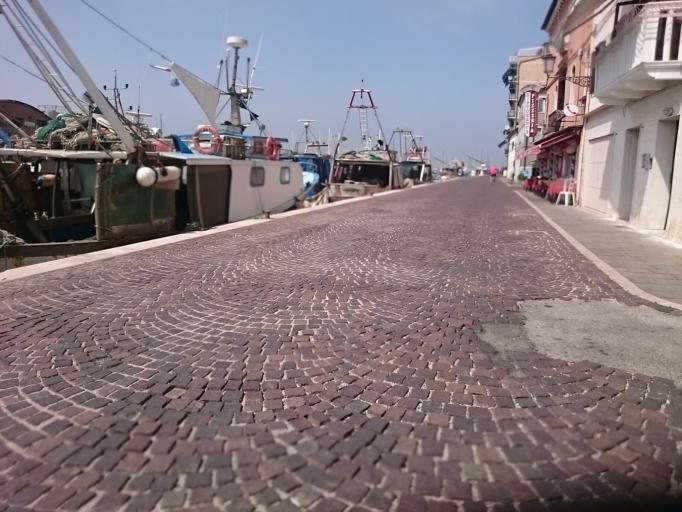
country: IT
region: Veneto
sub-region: Provincia di Venezia
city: Chioggia
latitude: 45.2222
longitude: 12.2780
